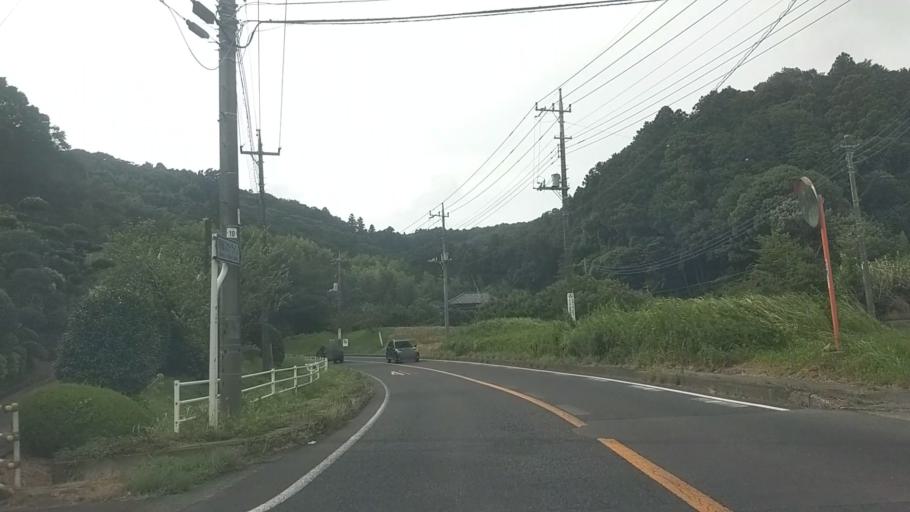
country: JP
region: Chiba
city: Kimitsu
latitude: 35.3133
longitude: 139.9611
